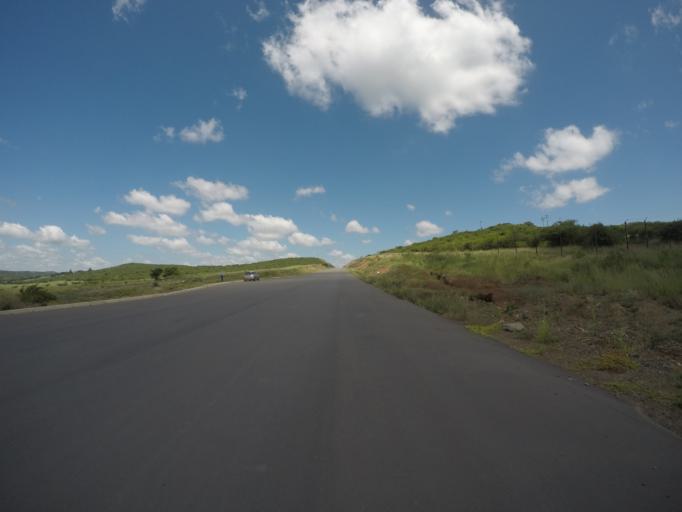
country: ZA
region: KwaZulu-Natal
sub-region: uThungulu District Municipality
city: Empangeni
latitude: -28.6203
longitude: 31.7564
